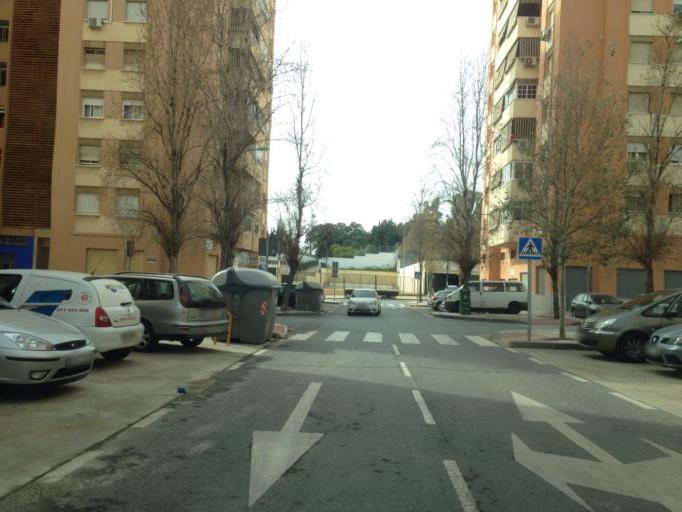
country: ES
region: Andalusia
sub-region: Provincia de Malaga
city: Malaga
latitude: 36.7324
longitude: -4.4306
